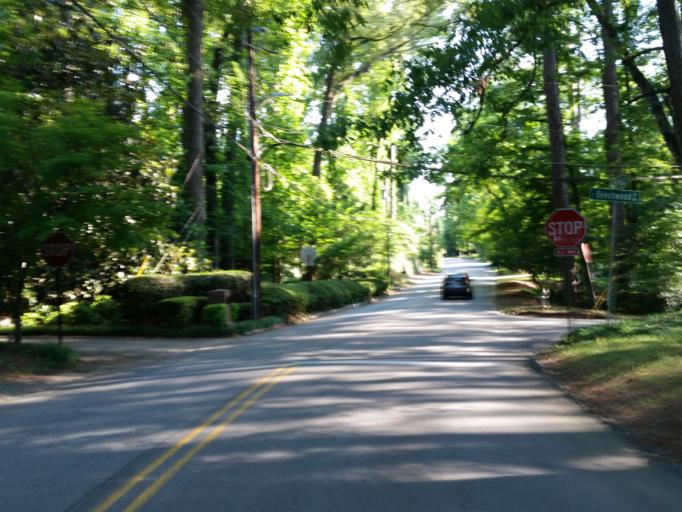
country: US
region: Georgia
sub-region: Cobb County
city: Vinings
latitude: 33.8538
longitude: -84.4222
